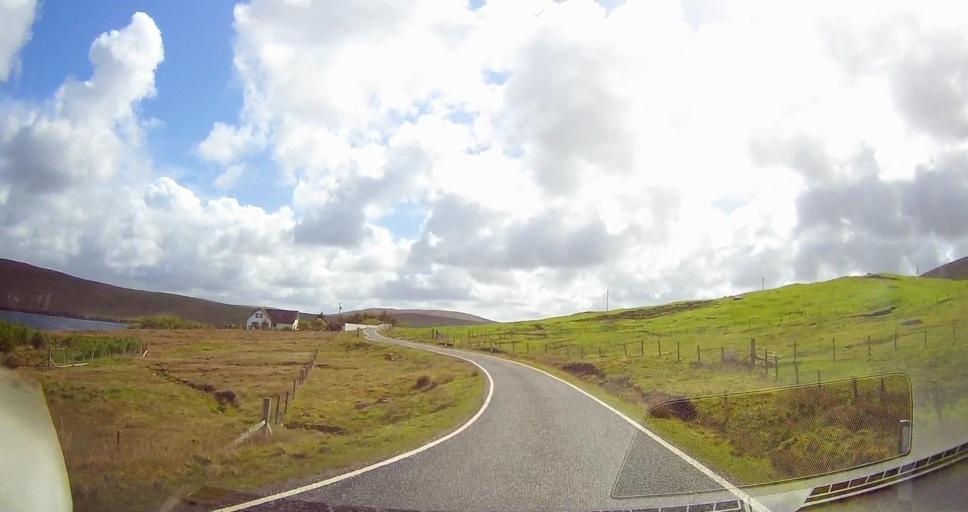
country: GB
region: Scotland
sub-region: Shetland Islands
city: Lerwick
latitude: 60.5379
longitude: -1.3565
